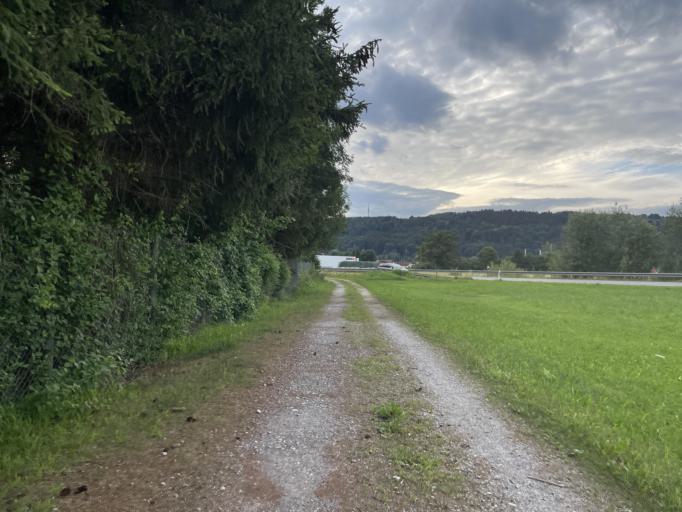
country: DE
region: Bavaria
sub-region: Upper Bavaria
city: Peissenberg
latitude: 47.7807
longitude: 11.0626
